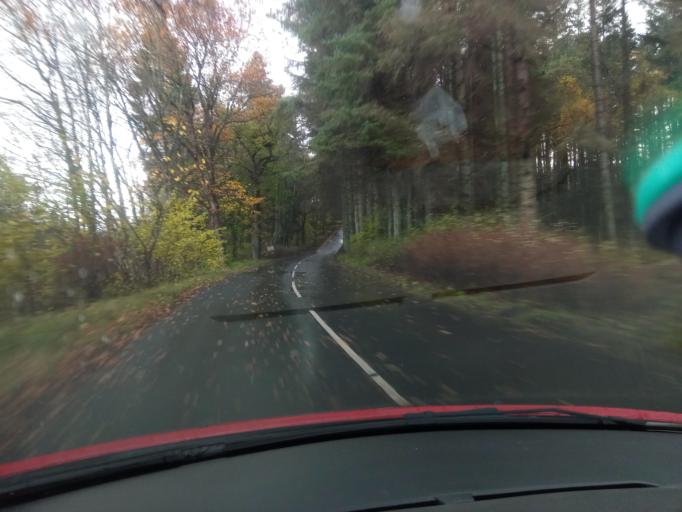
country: GB
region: England
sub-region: Northumberland
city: Birtley
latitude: 55.1017
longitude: -2.2287
